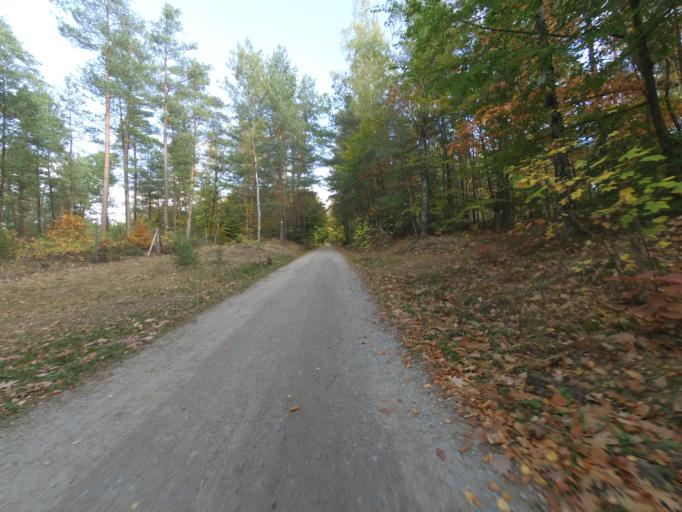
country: DE
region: Saxony
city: Albertstadt
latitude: 51.0914
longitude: 13.7905
